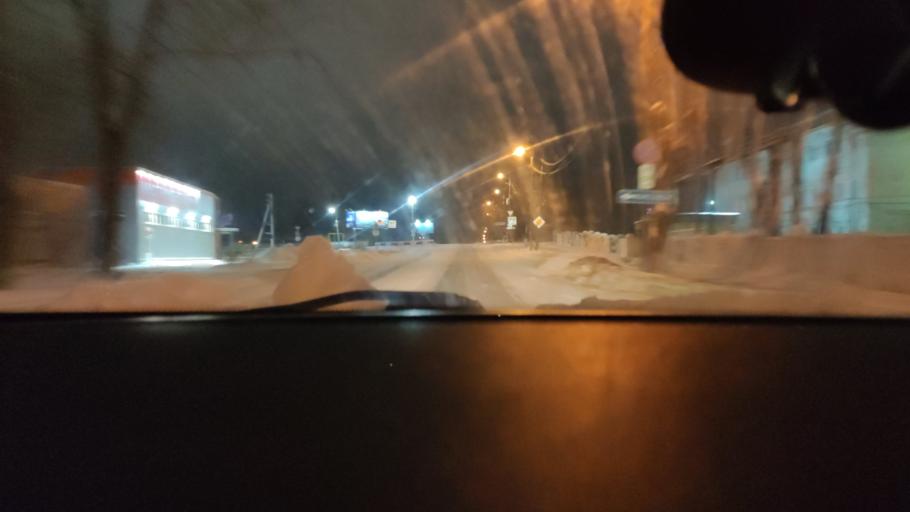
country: RU
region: Perm
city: Krasnokamsk
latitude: 58.0816
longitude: 55.7704
